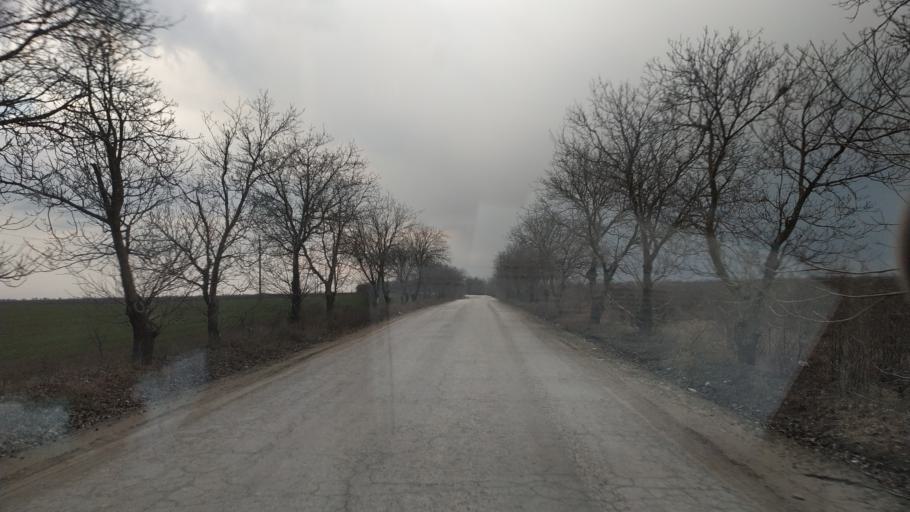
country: MD
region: Telenesti
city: Grigoriopol
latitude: 47.0398
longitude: 29.2938
